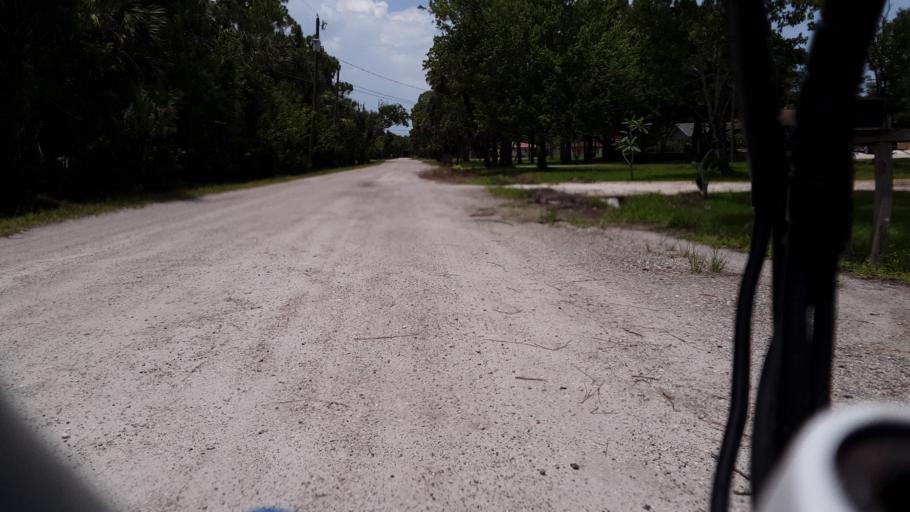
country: US
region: Florida
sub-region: Brevard County
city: Malabar
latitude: 27.9895
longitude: -80.6018
